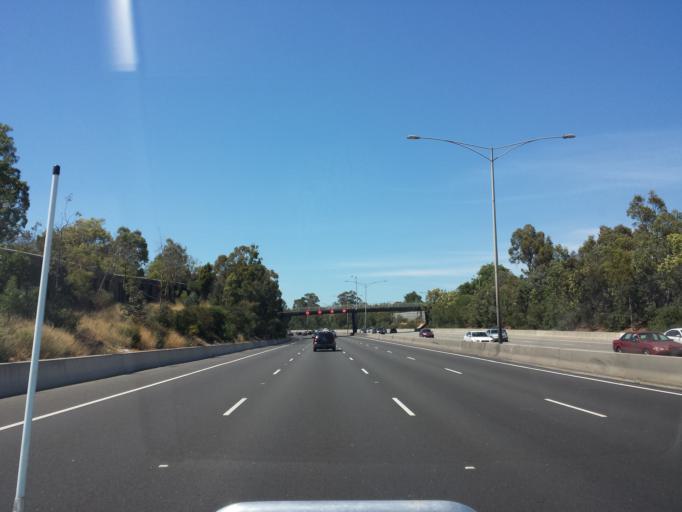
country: AU
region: Victoria
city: Carnegie
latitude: -37.8720
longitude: 145.0653
